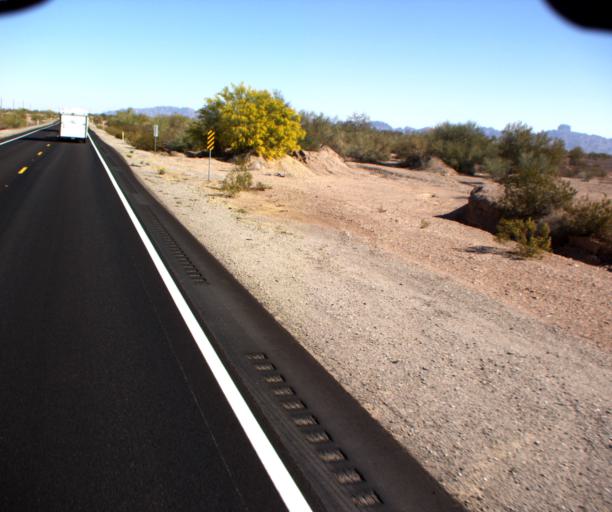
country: US
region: Arizona
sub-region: Yuma County
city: Wellton
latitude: 32.9871
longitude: -114.2881
